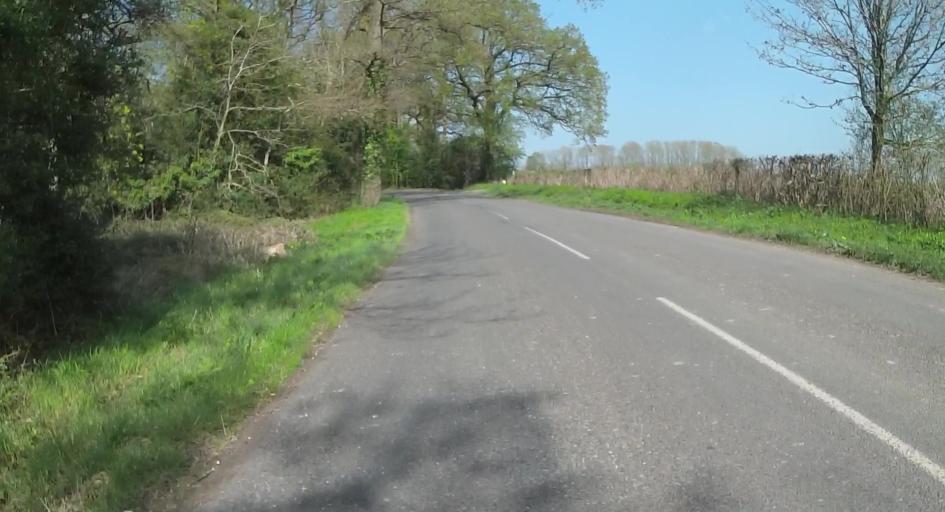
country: GB
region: England
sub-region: Hampshire
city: Basingstoke
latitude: 51.3123
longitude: -1.0831
